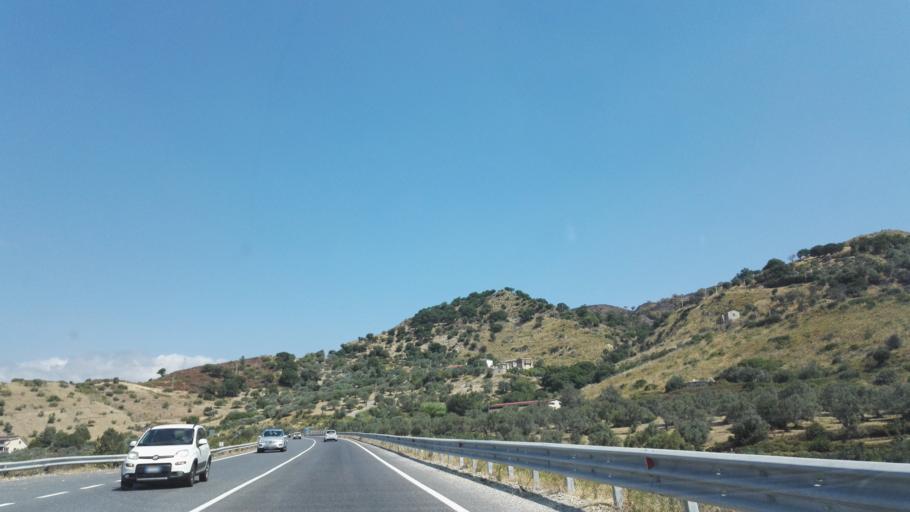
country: IT
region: Calabria
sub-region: Provincia di Reggio Calabria
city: Gioiosa Ionica
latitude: 38.3294
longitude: 16.2913
